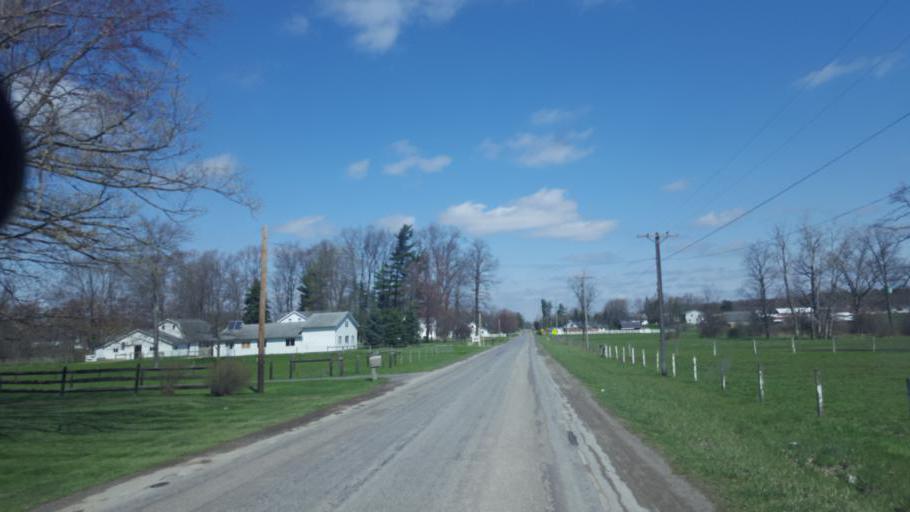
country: US
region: Ohio
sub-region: Geauga County
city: Middlefield
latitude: 41.4448
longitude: -81.0807
